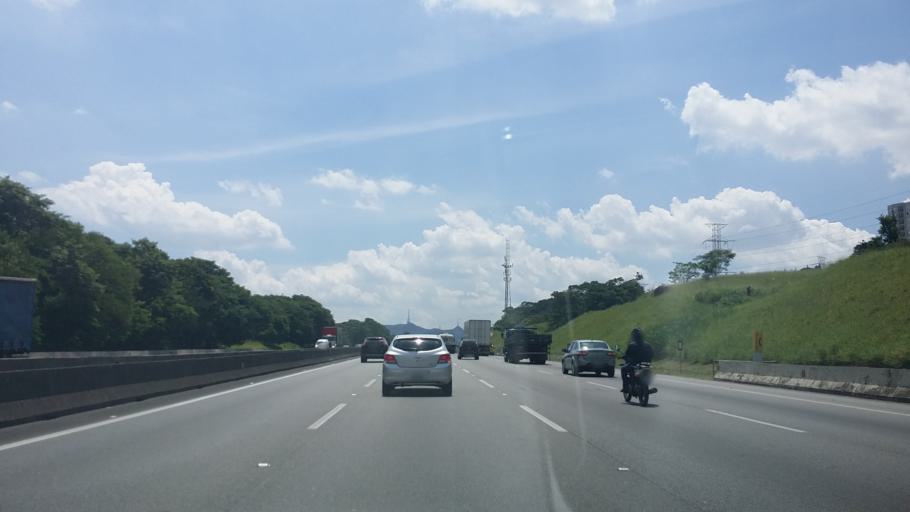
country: BR
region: Sao Paulo
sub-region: Osasco
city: Osasco
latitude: -23.5036
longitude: -46.7246
